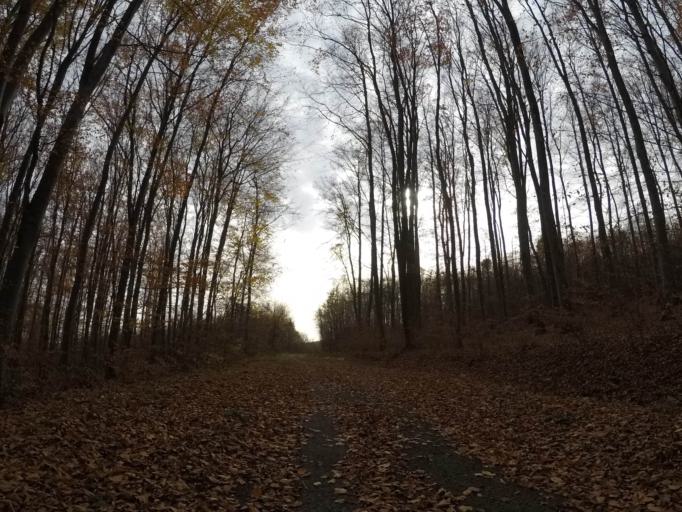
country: SK
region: Presovsky
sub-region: Okres Presov
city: Presov
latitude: 48.9670
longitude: 21.1837
